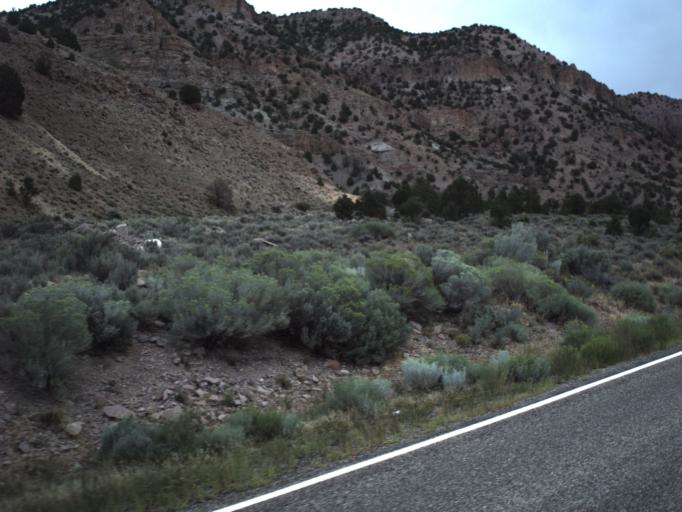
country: US
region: Utah
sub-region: Piute County
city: Junction
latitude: 38.1965
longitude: -112.1206
